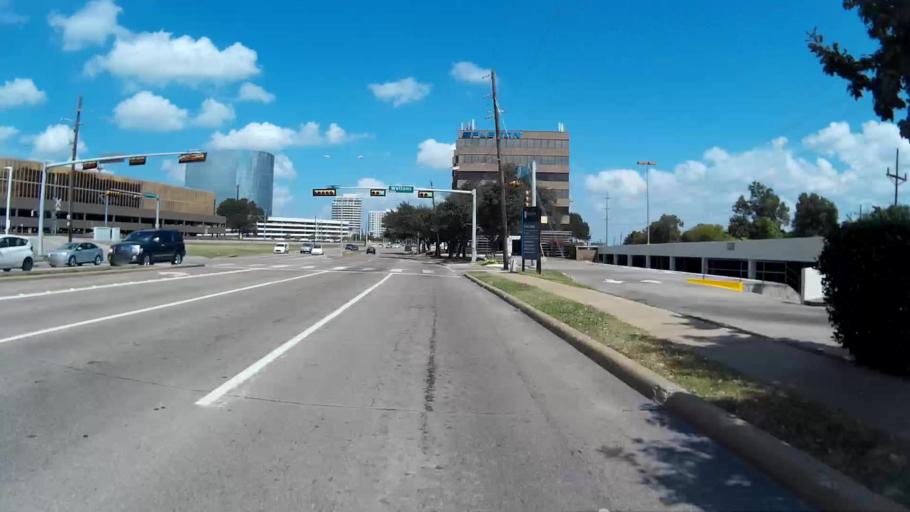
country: US
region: Texas
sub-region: Dallas County
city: University Park
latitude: 32.8632
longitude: -96.7673
